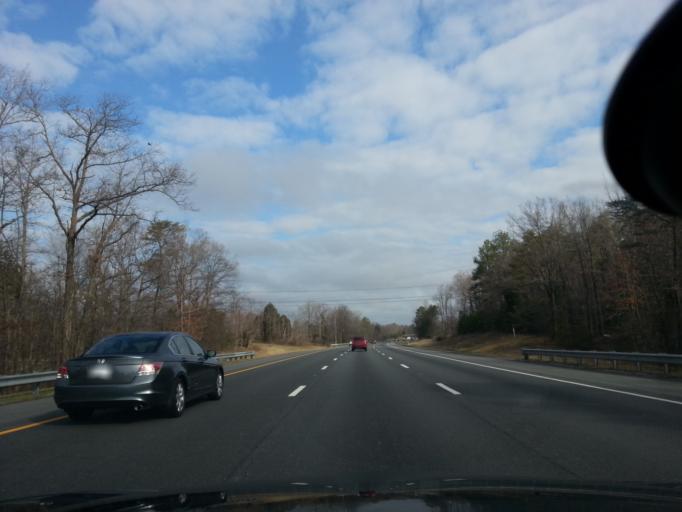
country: US
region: Virginia
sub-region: Spotsylvania County
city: Spotsylvania Courthouse
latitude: 38.0819
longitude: -77.5150
